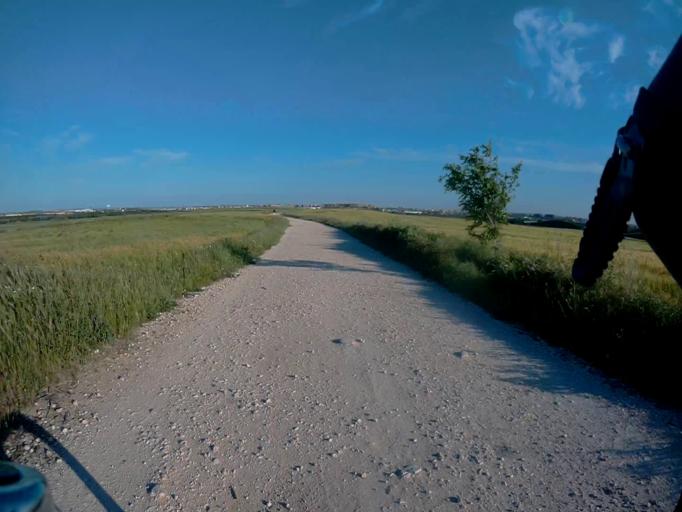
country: ES
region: Madrid
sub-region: Provincia de Madrid
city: Alcorcon
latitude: 40.3252
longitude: -3.8149
